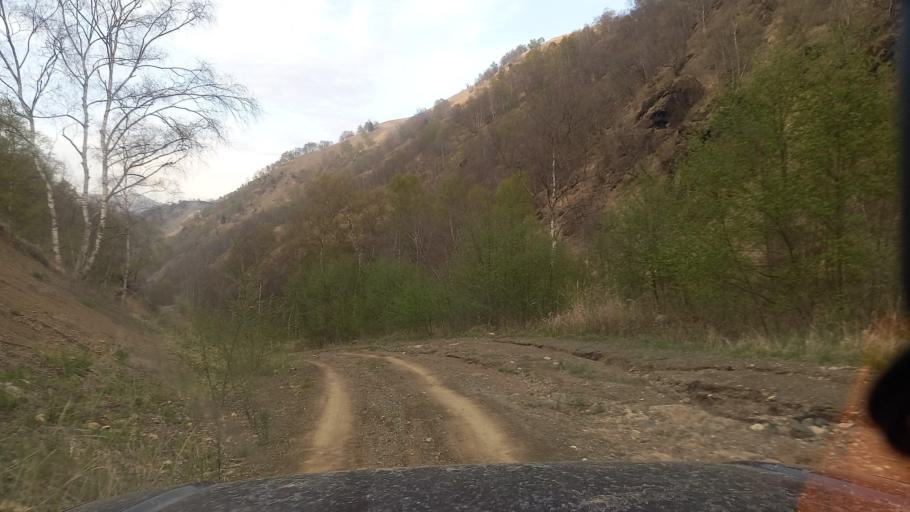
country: RU
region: Kabardino-Balkariya
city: Kamennomostskoye
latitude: 43.6983
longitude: 42.8416
